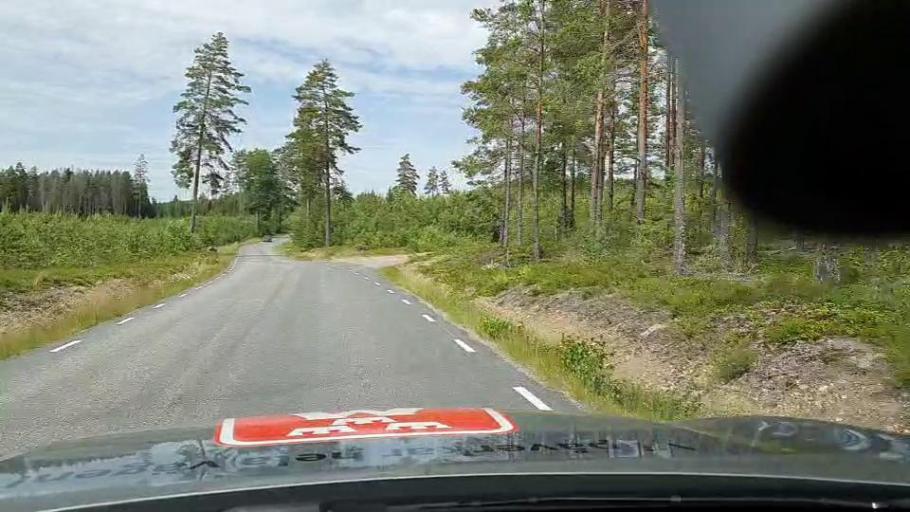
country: SE
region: Soedermanland
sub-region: Eskilstuna Kommun
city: Arla
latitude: 59.2363
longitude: 16.7229
